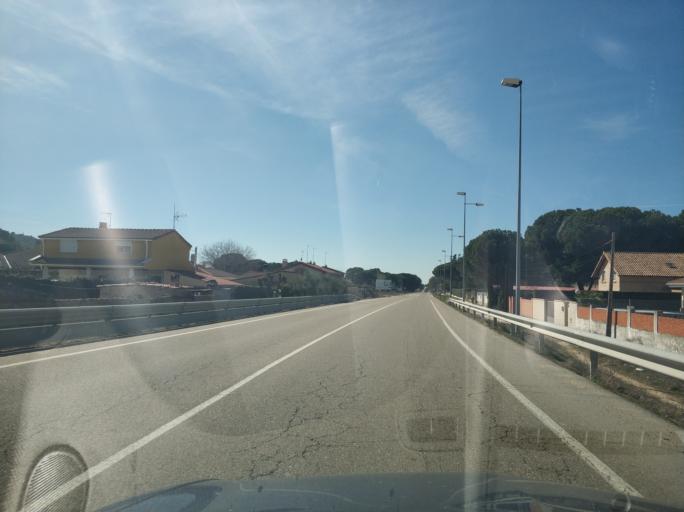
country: ES
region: Castille and Leon
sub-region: Provincia de Valladolid
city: Tudela de Duero
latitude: 41.5765
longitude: -4.5804
